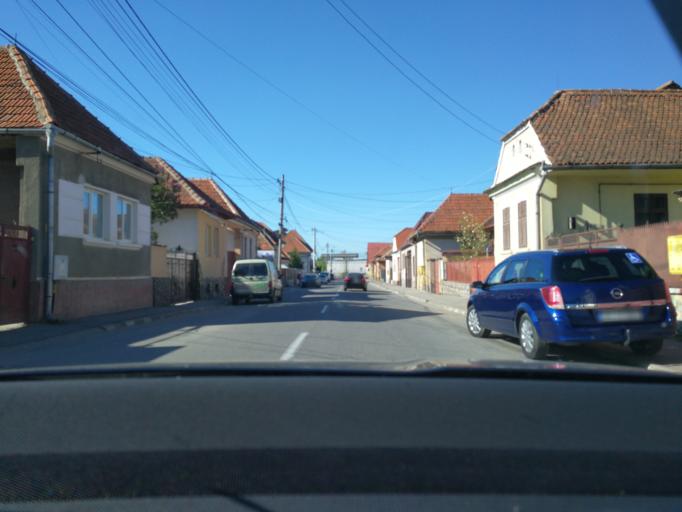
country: RO
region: Brasov
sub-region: Oras Rasnov
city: Rasnov
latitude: 45.5880
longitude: 25.4585
